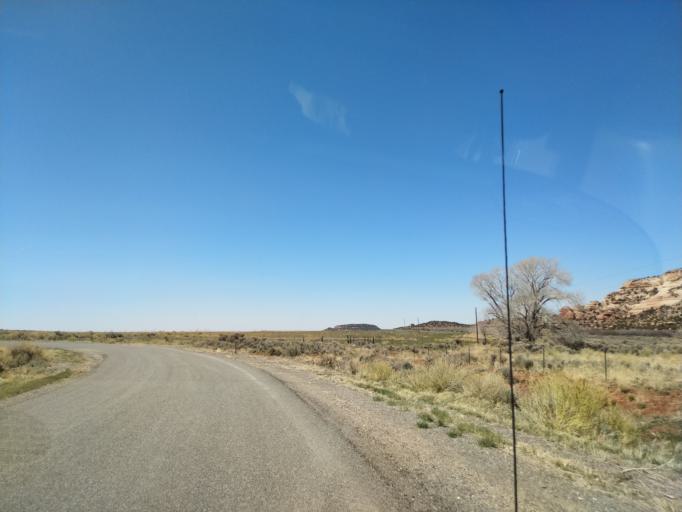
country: US
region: Colorado
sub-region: Mesa County
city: Loma
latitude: 38.9537
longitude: -109.0302
